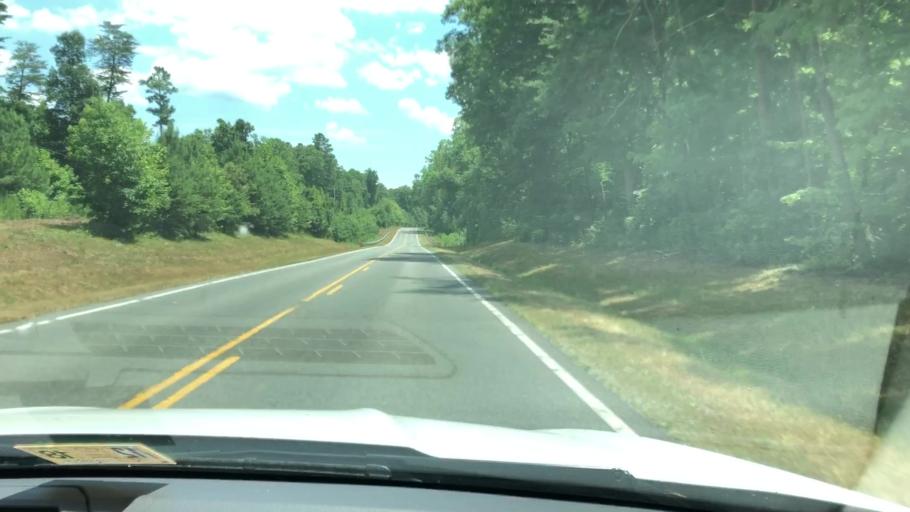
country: US
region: Virginia
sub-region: Lancaster County
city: Lancaster
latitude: 37.8216
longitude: -76.5554
